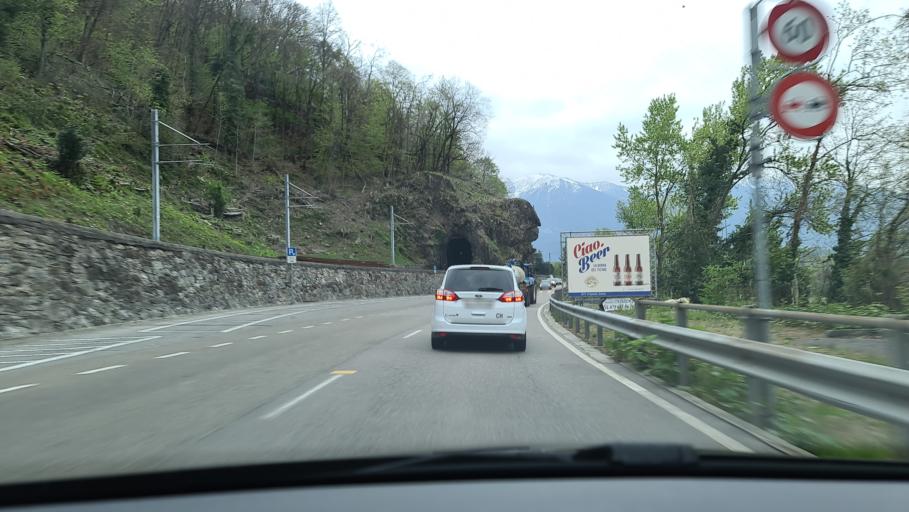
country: CH
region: Ticino
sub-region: Locarno District
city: Losone
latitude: 46.1793
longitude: 8.7610
